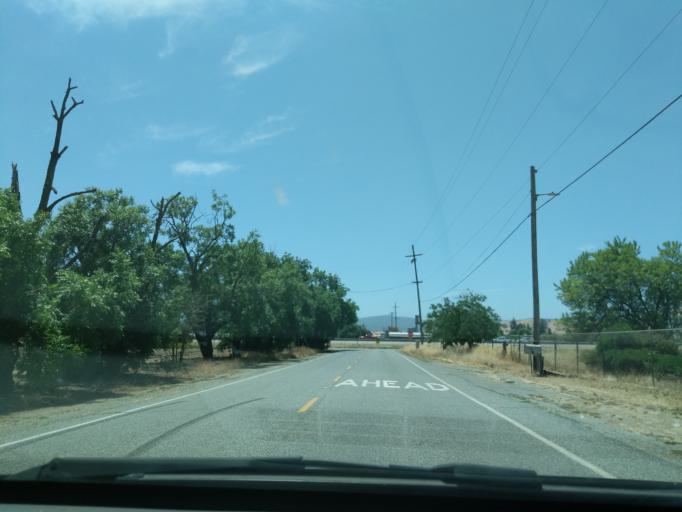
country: US
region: California
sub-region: Santa Clara County
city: San Martin
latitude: 37.0540
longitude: -121.5805
